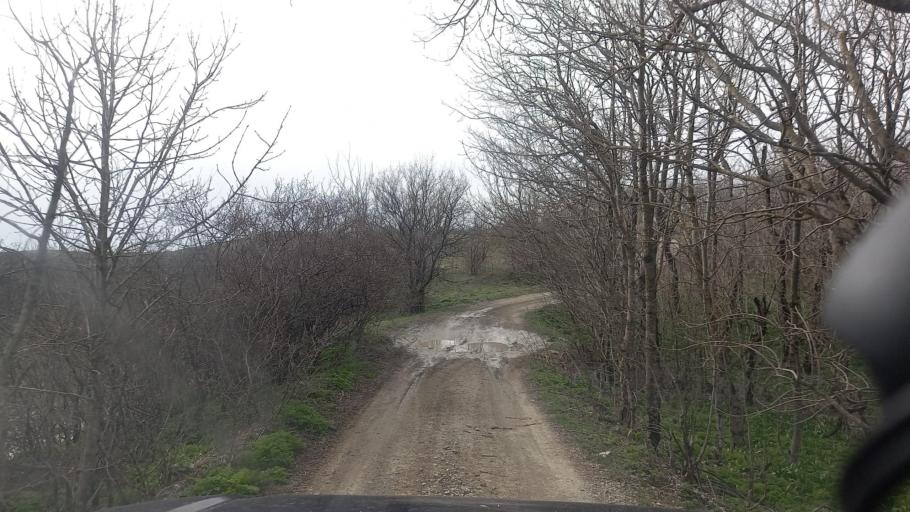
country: RU
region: Krasnodarskiy
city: Divnomorskoye
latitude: 44.6130
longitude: 38.2302
